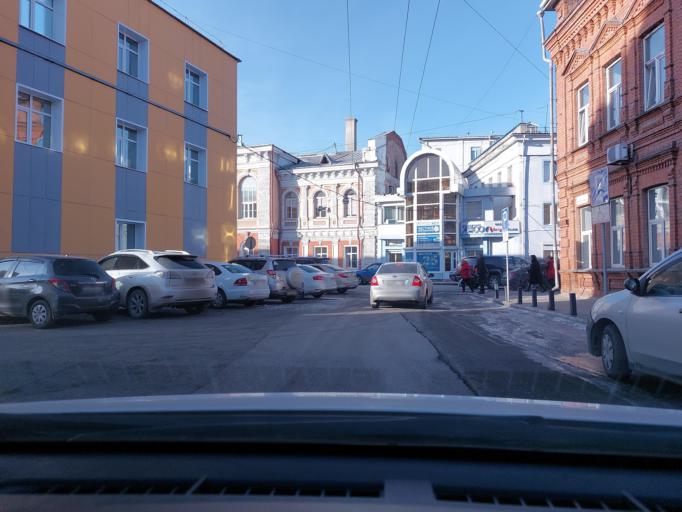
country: RU
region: Irkutsk
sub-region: Irkutskiy Rayon
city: Irkutsk
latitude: 52.2882
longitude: 104.2836
